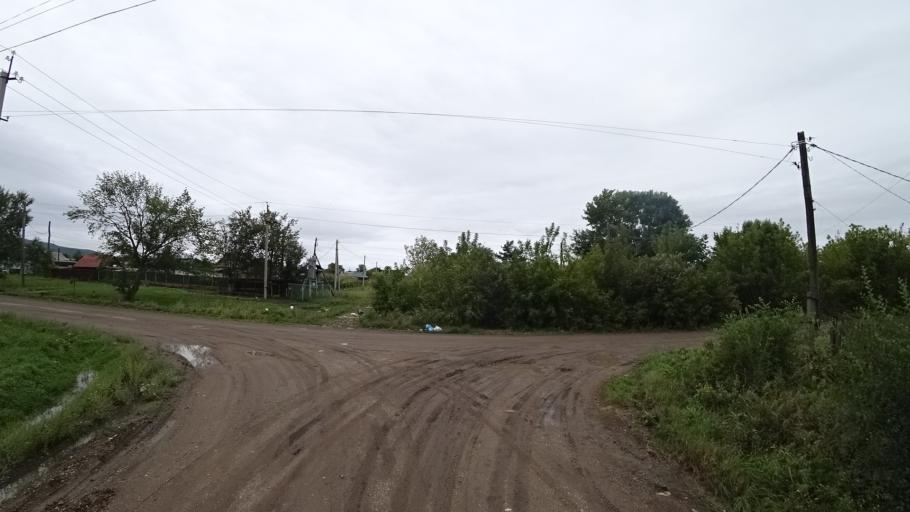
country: RU
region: Primorskiy
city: Chernigovka
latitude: 44.3373
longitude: 132.5597
